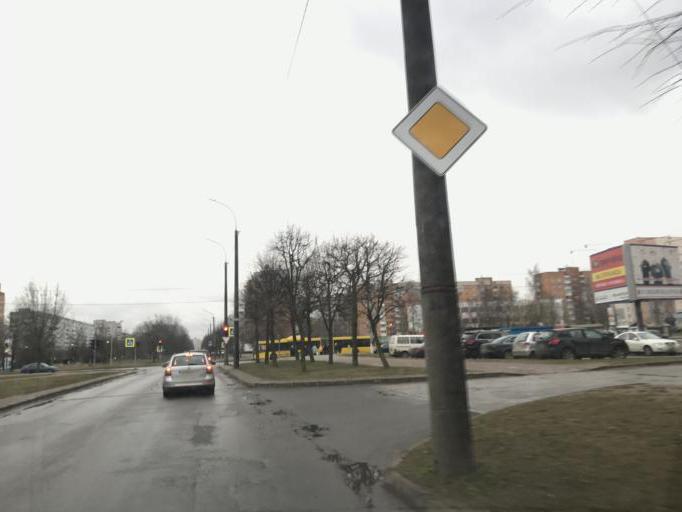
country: BY
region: Mogilev
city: Mahilyow
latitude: 53.8749
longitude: 30.3305
